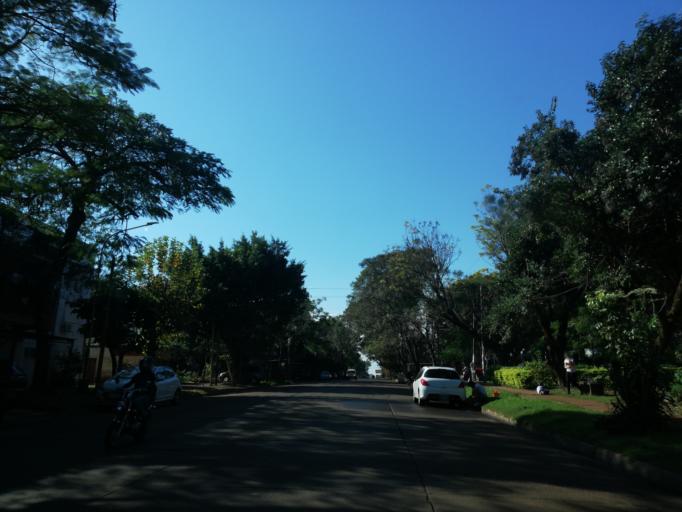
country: AR
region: Misiones
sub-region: Departamento de Capital
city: Posadas
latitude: -27.3687
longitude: -55.9497
